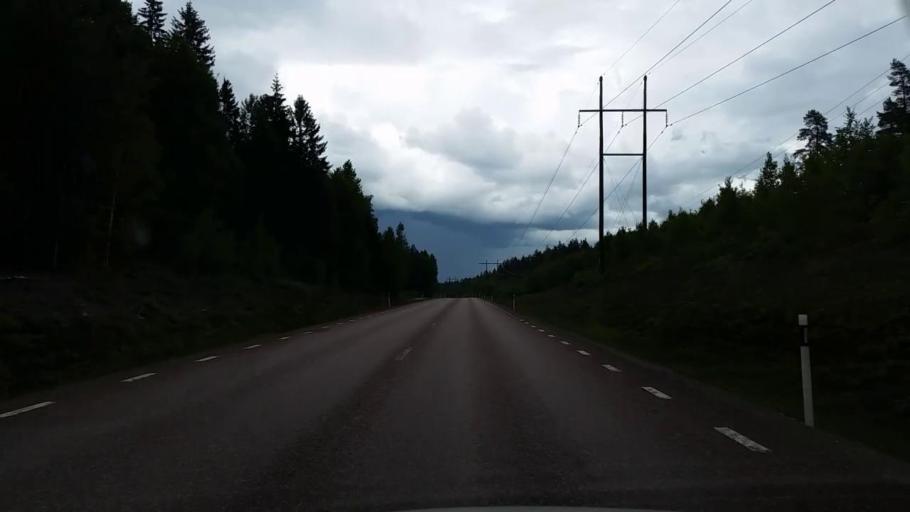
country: SE
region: Gaevleborg
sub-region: Hofors Kommun
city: Hofors
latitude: 60.5196
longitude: 16.4433
